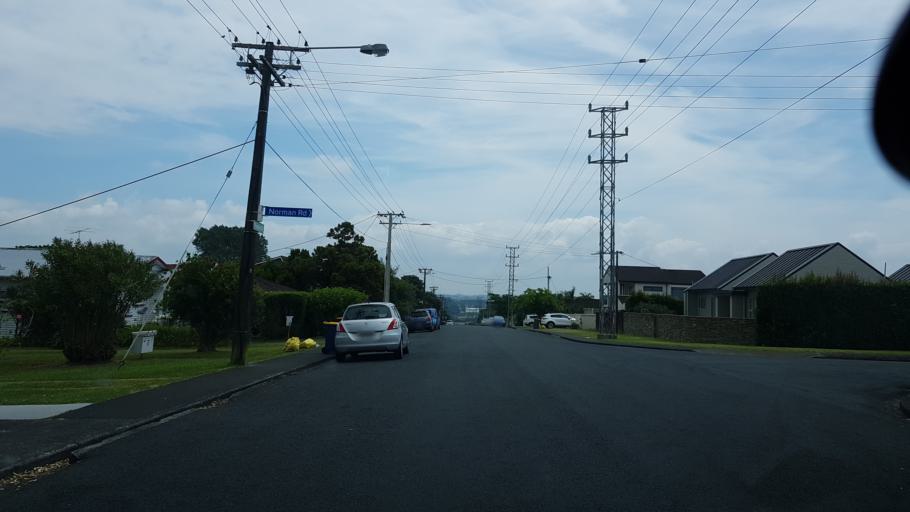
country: NZ
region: Auckland
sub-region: Auckland
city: North Shore
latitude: -36.8009
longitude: 174.7748
